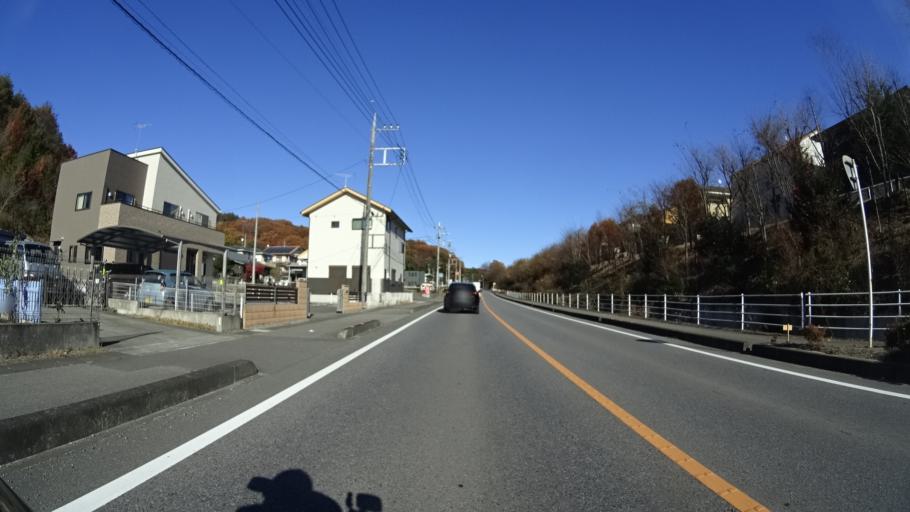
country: JP
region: Tochigi
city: Utsunomiya-shi
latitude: 36.5975
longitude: 139.8110
